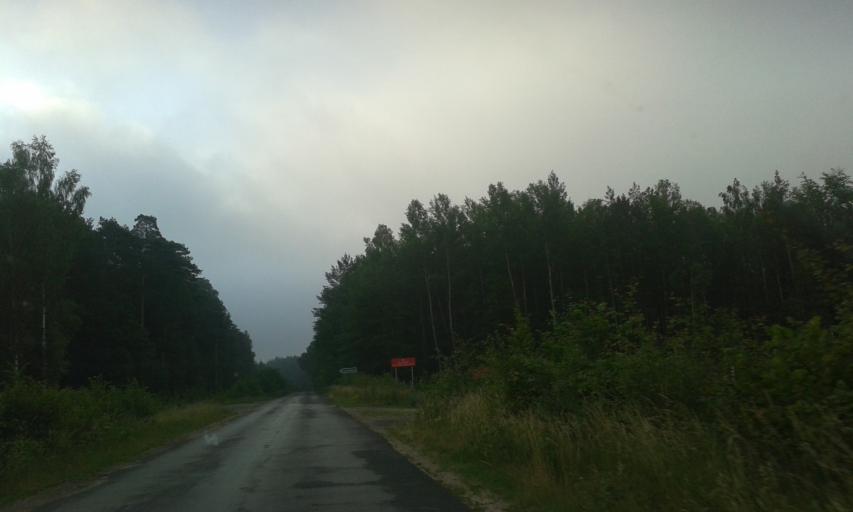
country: PL
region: Kujawsko-Pomorskie
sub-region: Powiat sepolenski
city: Sypniewo
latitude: 53.4538
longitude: 17.3507
